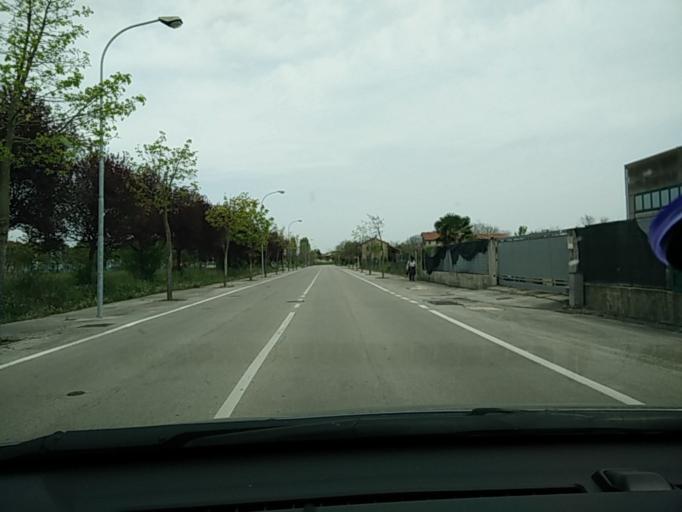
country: IT
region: Veneto
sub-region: Provincia di Venezia
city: Musile di Piave
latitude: 45.6191
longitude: 12.5440
